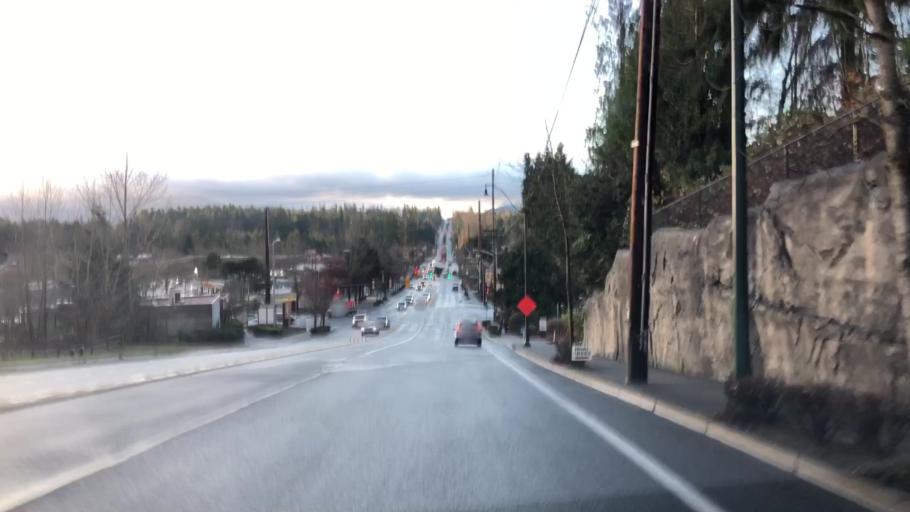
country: US
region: Washington
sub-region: King County
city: City of Sammamish
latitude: 47.6179
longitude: -122.0356
